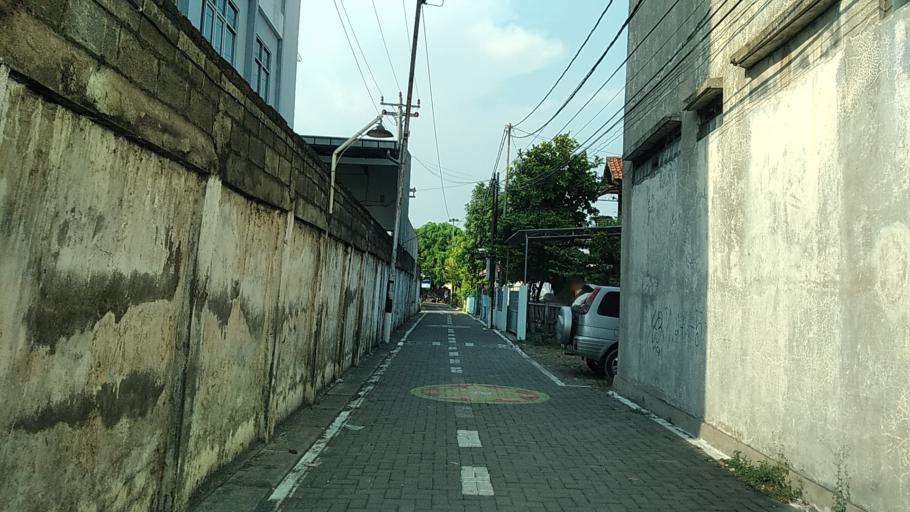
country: ID
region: Central Java
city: Semarang
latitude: -7.0065
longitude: 110.4573
